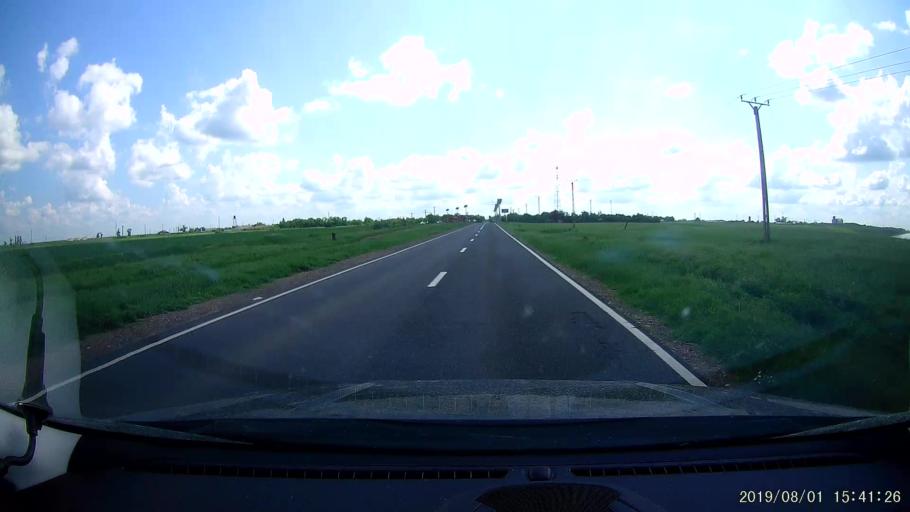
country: RO
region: Braila
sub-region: Comuna Baraganul
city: Baraganul
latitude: 44.8227
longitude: 27.5263
